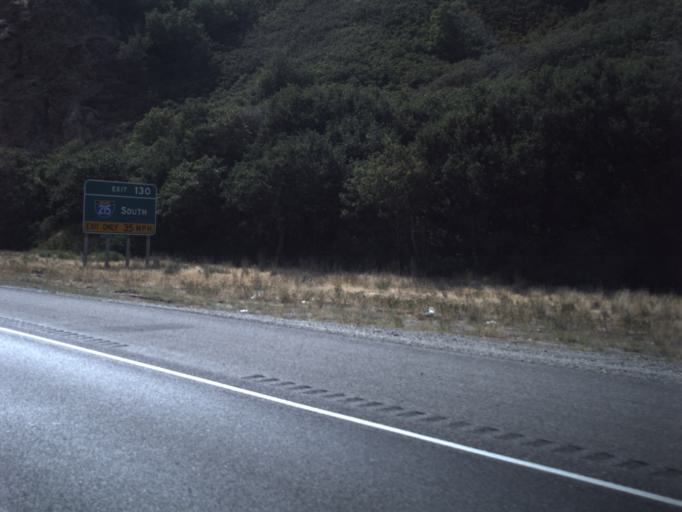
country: US
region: Utah
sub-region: Salt Lake County
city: East Millcreek
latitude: 40.7184
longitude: -111.7832
